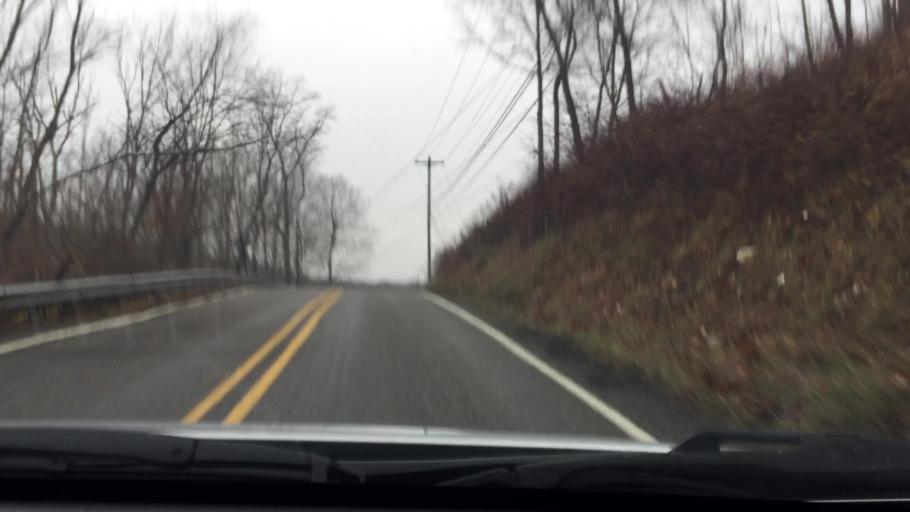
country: US
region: Pennsylvania
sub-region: Beaver County
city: Conway
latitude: 40.6795
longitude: -80.1967
